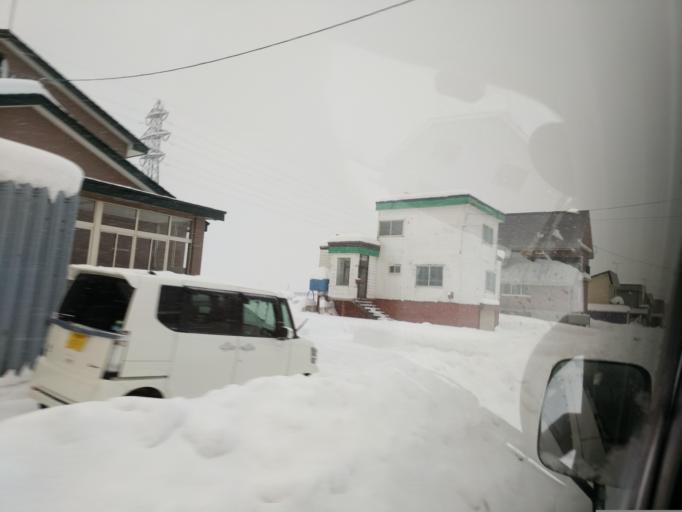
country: JP
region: Hokkaido
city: Niseko Town
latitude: 42.8921
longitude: 140.7450
